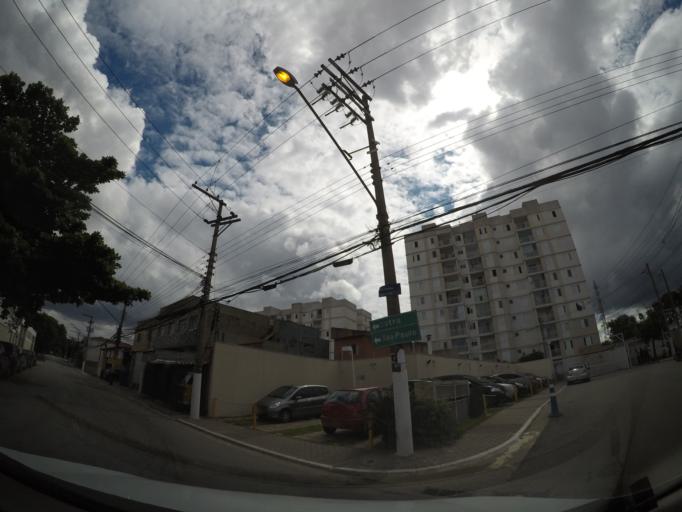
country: BR
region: Sao Paulo
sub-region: Guarulhos
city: Guarulhos
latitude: -23.4891
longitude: -46.5539
